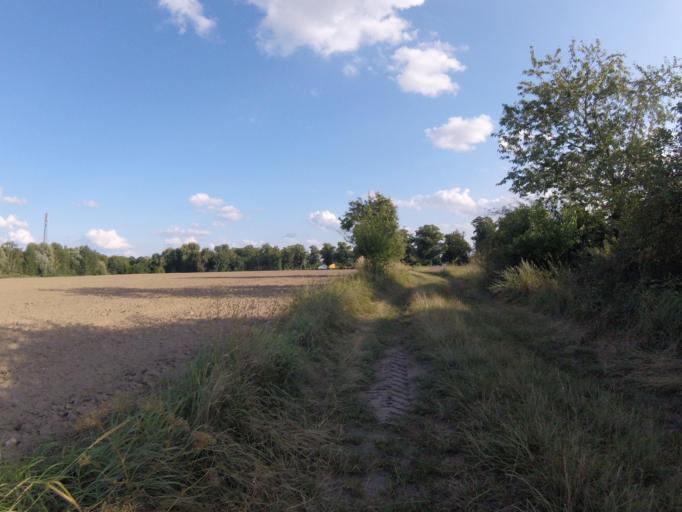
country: DE
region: Brandenburg
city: Mittenwalde
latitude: 52.2923
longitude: 13.5460
